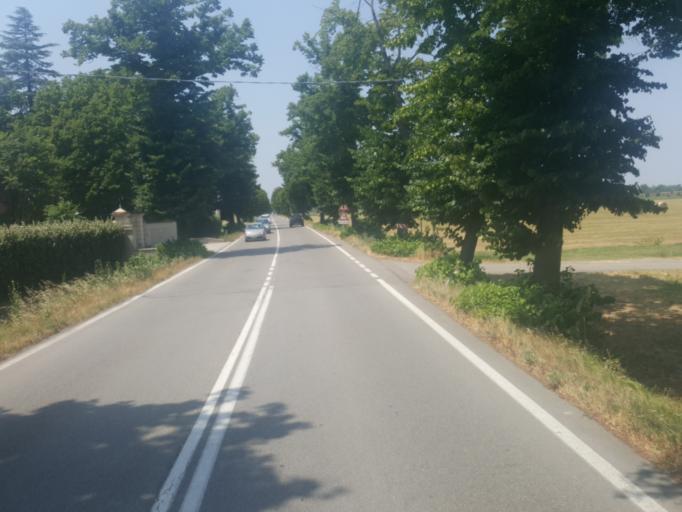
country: IT
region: Emilia-Romagna
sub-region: Provincia di Modena
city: Cavazzona
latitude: 44.5758
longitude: 11.1080
